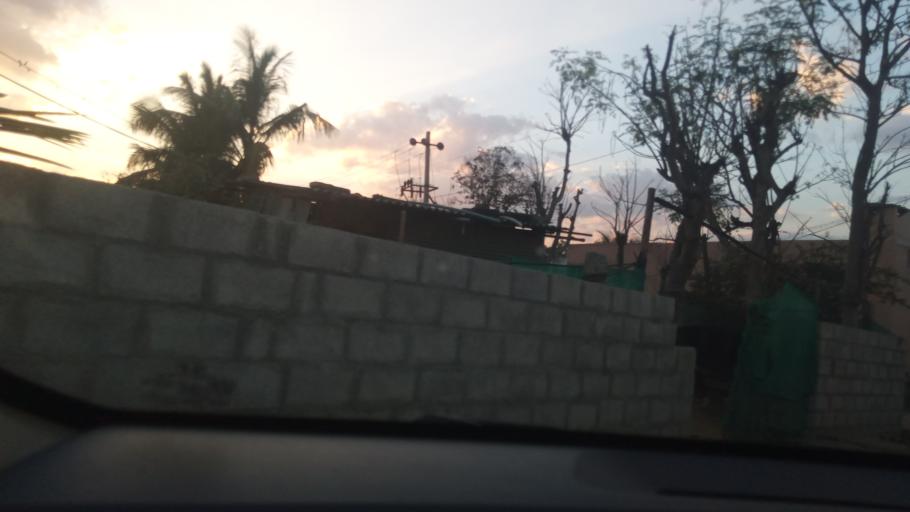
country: IN
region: Karnataka
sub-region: Bangalore Rural
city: Hoskote
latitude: 12.9779
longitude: 77.8011
